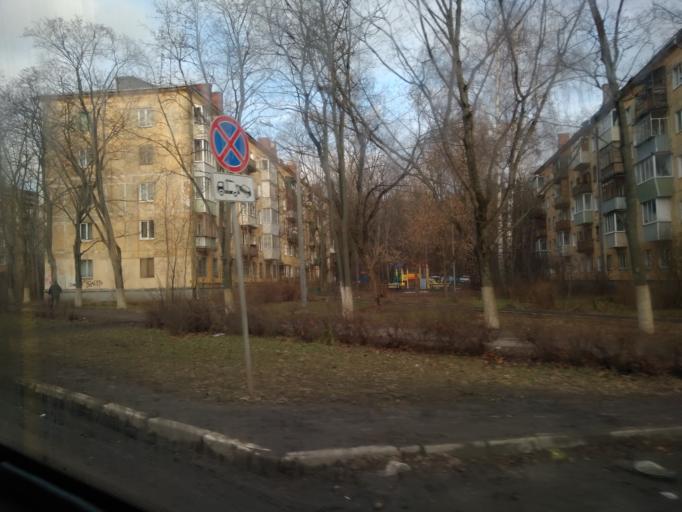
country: RU
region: Moskovskaya
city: Zhukovskiy
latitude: 55.5928
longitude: 38.1288
